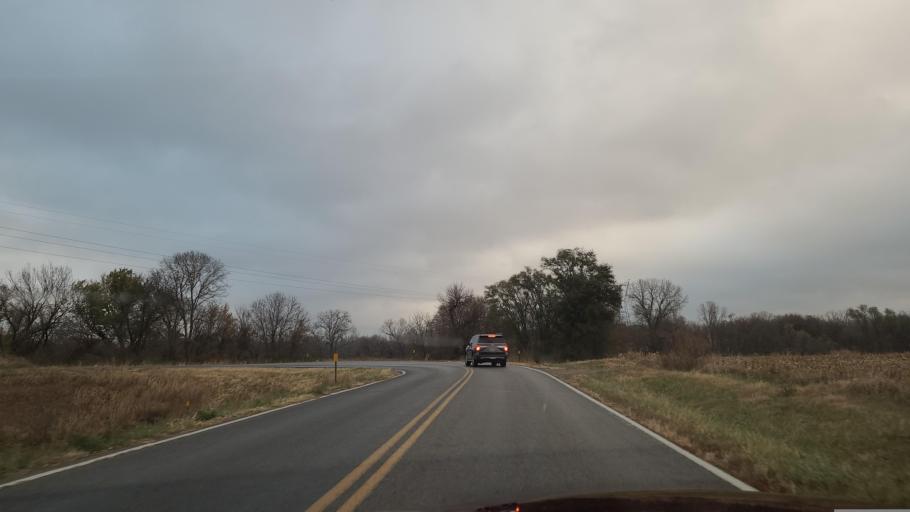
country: US
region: Kansas
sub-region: Douglas County
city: Lawrence
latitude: 38.9622
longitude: -95.2002
